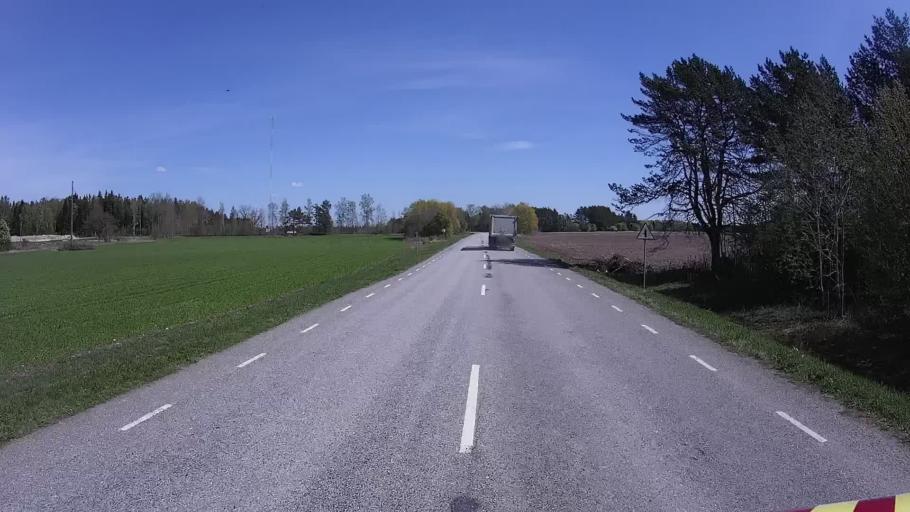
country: EE
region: Laeaene
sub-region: Ridala Parish
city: Uuemoisa
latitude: 58.9970
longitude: 23.7223
